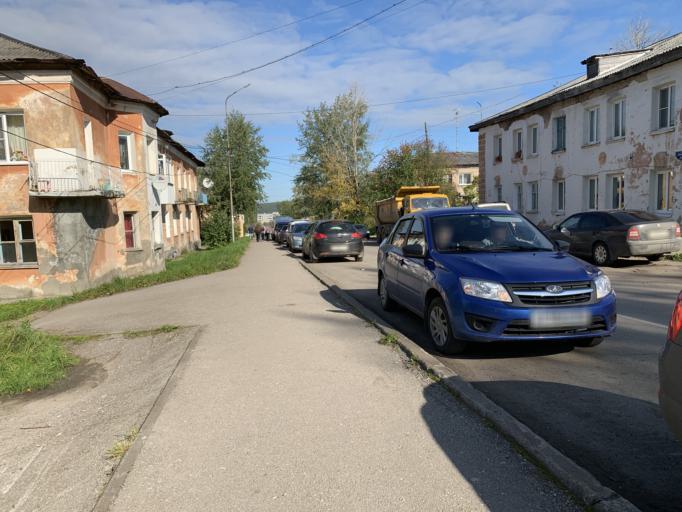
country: RU
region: Perm
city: Gubakha
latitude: 58.8424
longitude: 57.5537
